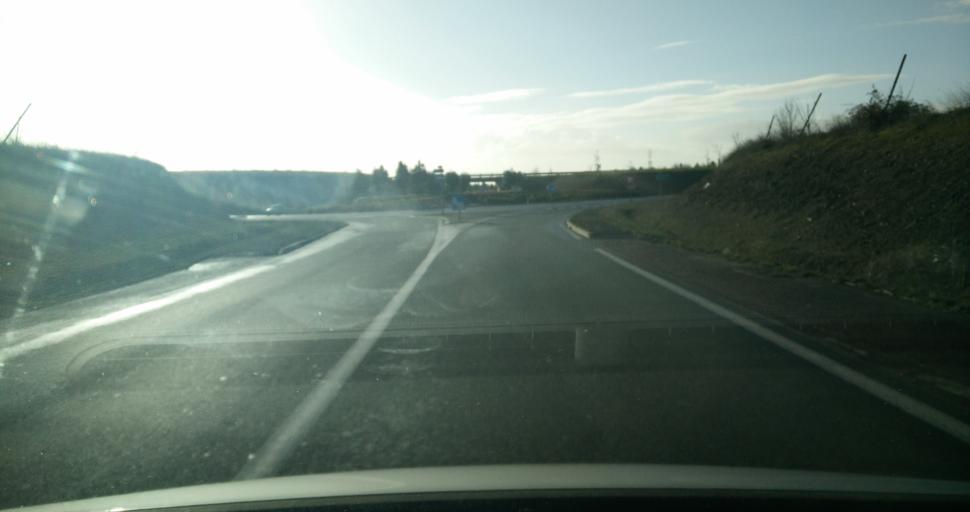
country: FR
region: Poitou-Charentes
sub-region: Departement de la Charente-Maritime
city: Saint-Xandre
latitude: 46.1824
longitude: -1.0919
